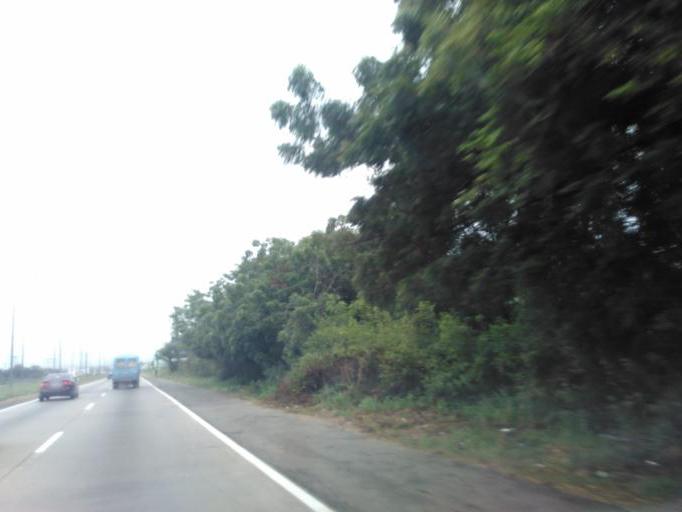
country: GH
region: Greater Accra
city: Medina Estates
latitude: 5.6485
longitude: -0.1094
